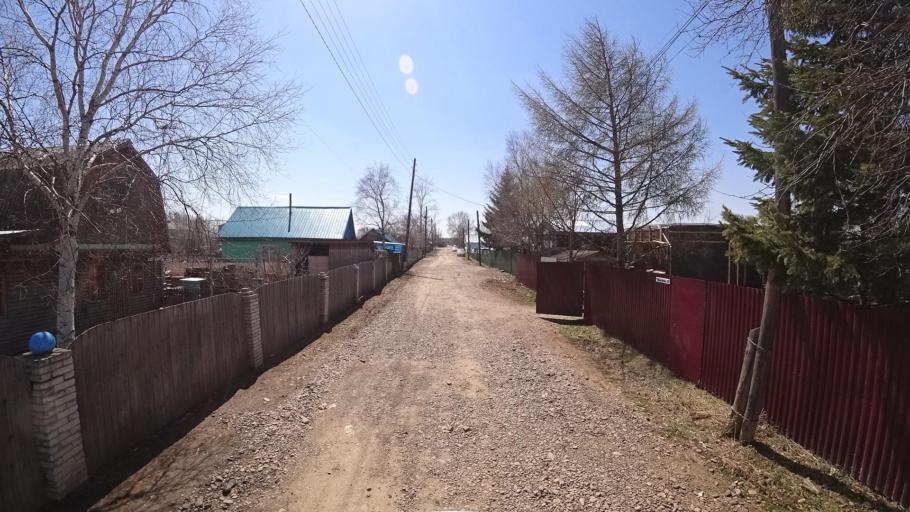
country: RU
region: Khabarovsk Krai
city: Khurba
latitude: 50.4062
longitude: 136.8869
